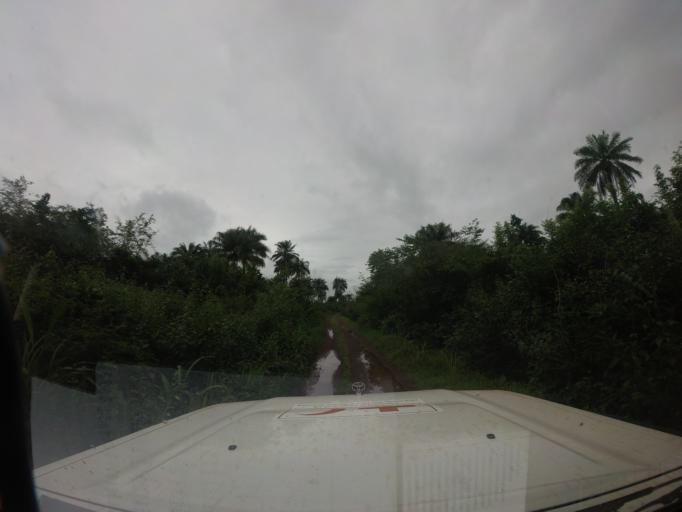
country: SL
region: Northern Province
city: Kambia
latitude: 9.1867
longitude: -12.8869
